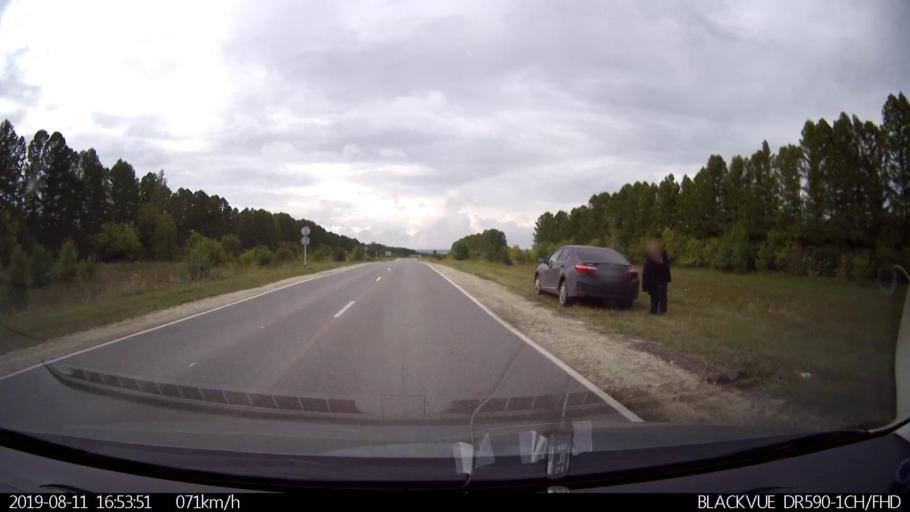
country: RU
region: Ulyanovsk
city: Mayna
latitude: 54.2669
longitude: 47.6685
